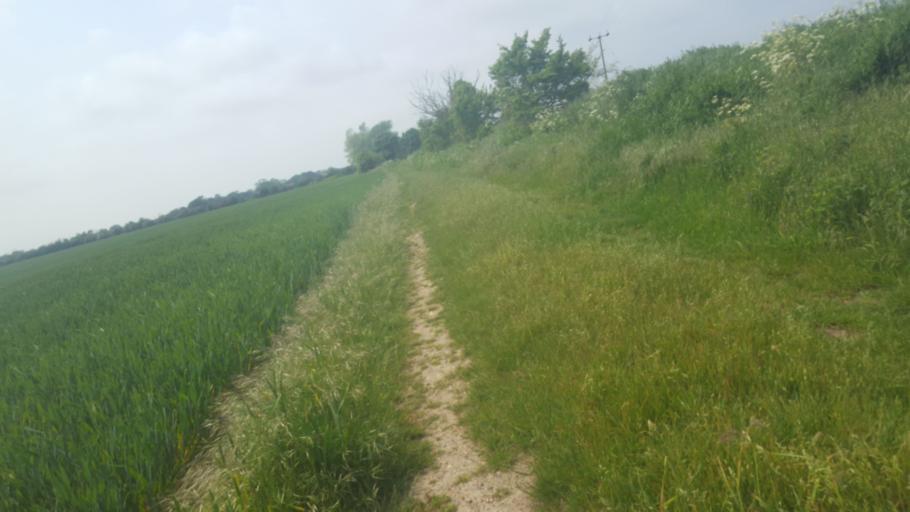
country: GB
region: England
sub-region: Essex
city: Saint Osyth
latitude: 51.7931
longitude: 1.0970
